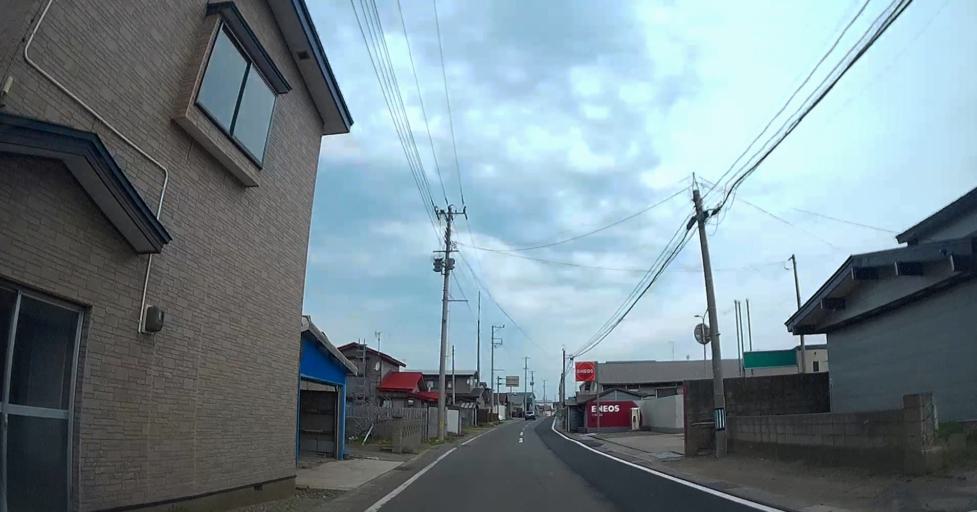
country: JP
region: Aomori
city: Shimokizukuri
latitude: 41.0269
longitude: 140.3258
